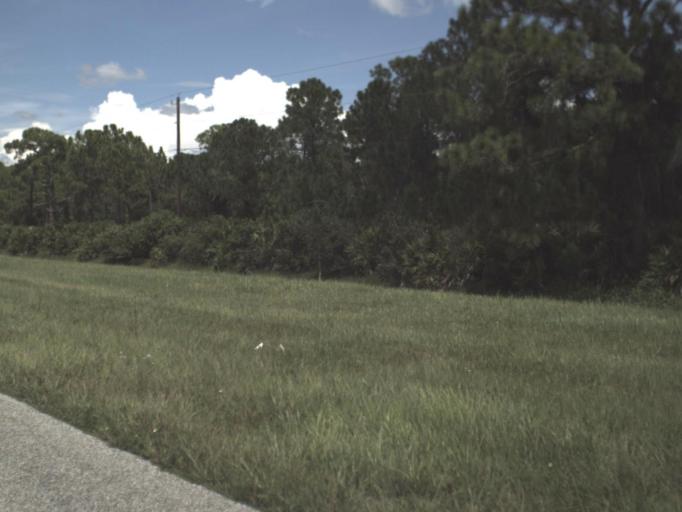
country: US
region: Florida
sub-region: Lee County
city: Burnt Store Marina
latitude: 26.8239
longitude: -81.9657
